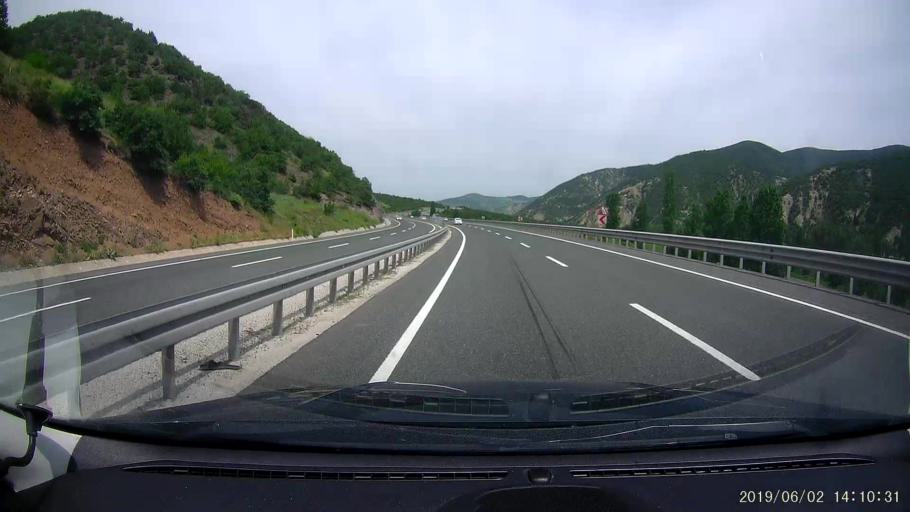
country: TR
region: Cankiri
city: Ilgaz
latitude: 40.9029
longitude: 33.7630
